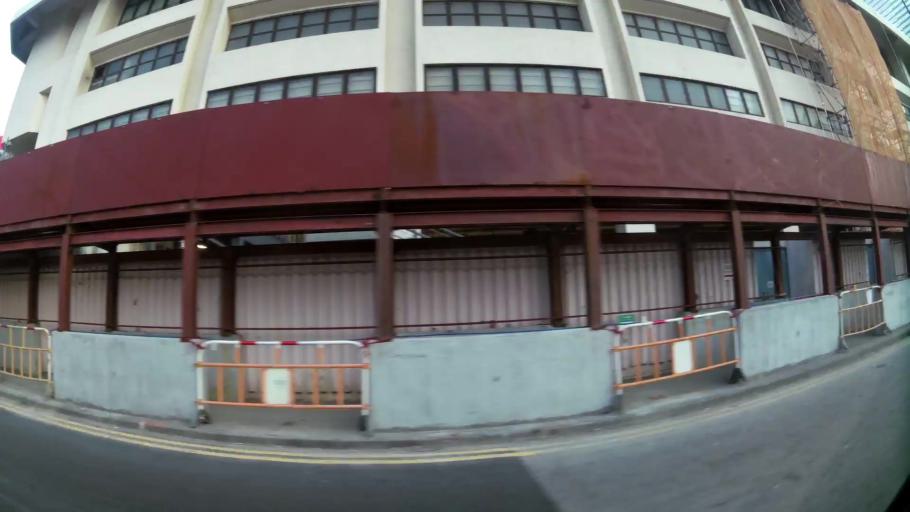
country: HK
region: Wanchai
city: Wan Chai
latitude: 22.2819
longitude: 114.1763
